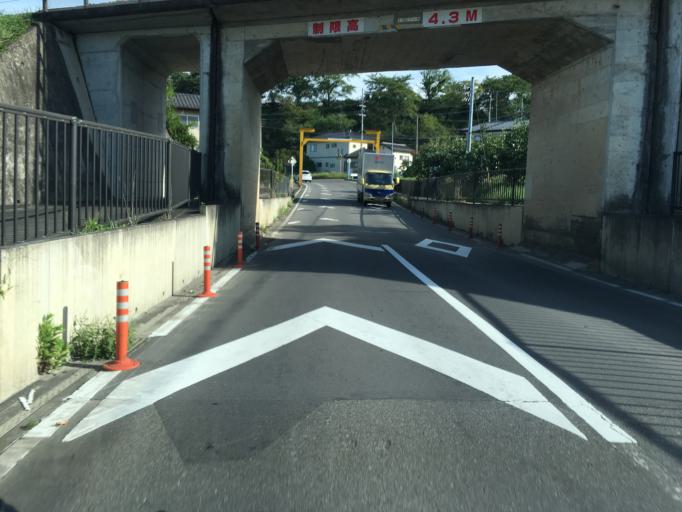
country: JP
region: Fukushima
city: Hobaramachi
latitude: 37.8099
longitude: 140.5439
